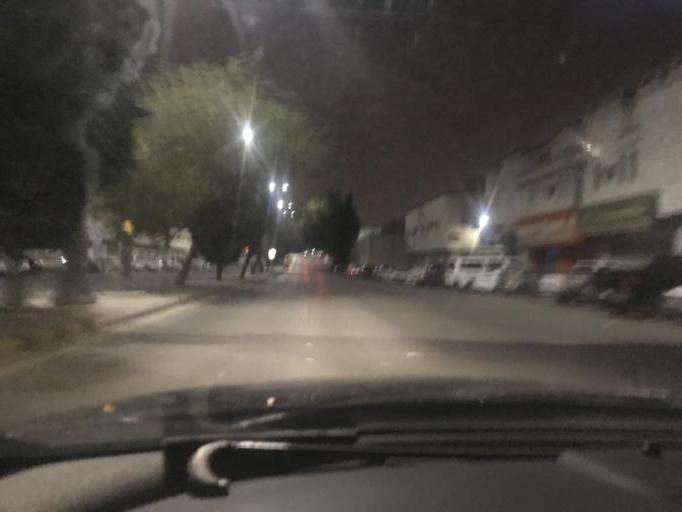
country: SA
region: Ar Riyad
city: Riyadh
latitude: 24.7293
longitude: 46.7636
